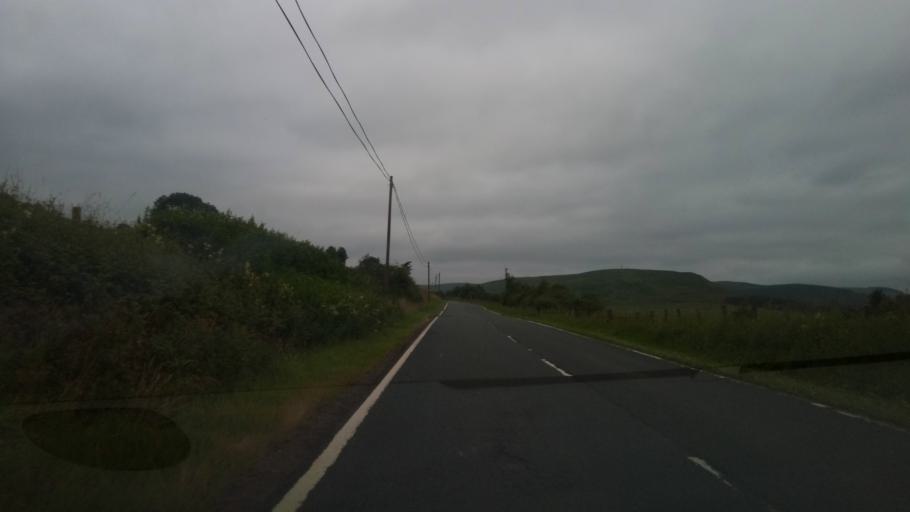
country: GB
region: Scotland
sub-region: The Scottish Borders
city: Hawick
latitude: 55.3444
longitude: -2.9273
